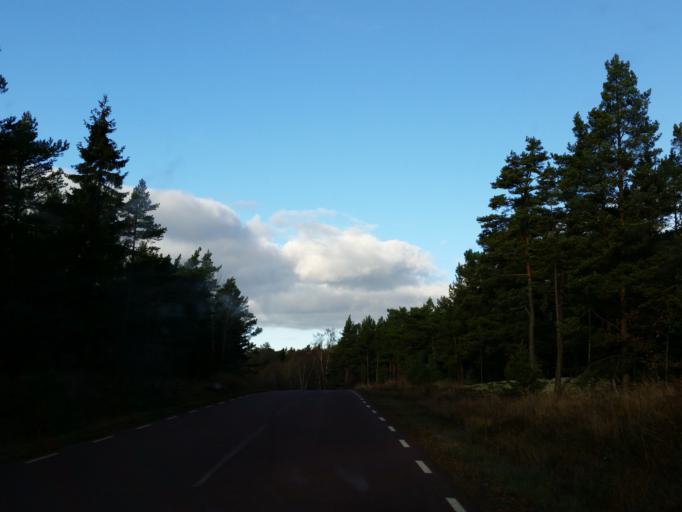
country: AX
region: Alands skaergard
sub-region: Foegloe
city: Foegloe
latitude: 60.0454
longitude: 20.5337
